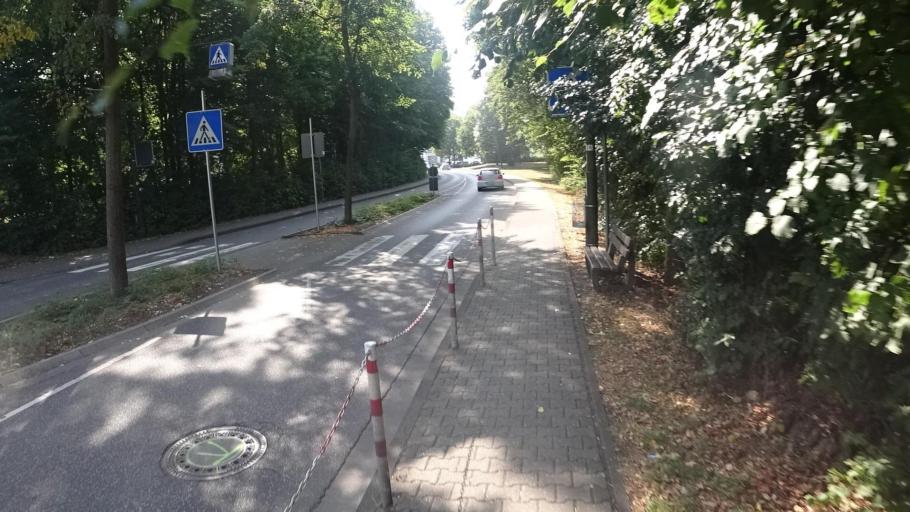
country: DE
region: Rheinland-Pfalz
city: Simmern
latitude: 49.9814
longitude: 7.5200
